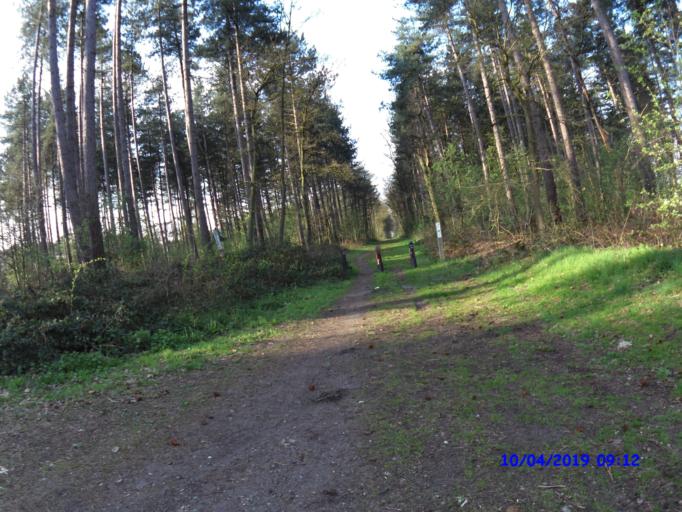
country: BE
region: Flanders
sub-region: Provincie Limburg
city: Leopoldsburg
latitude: 51.1063
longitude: 5.2466
